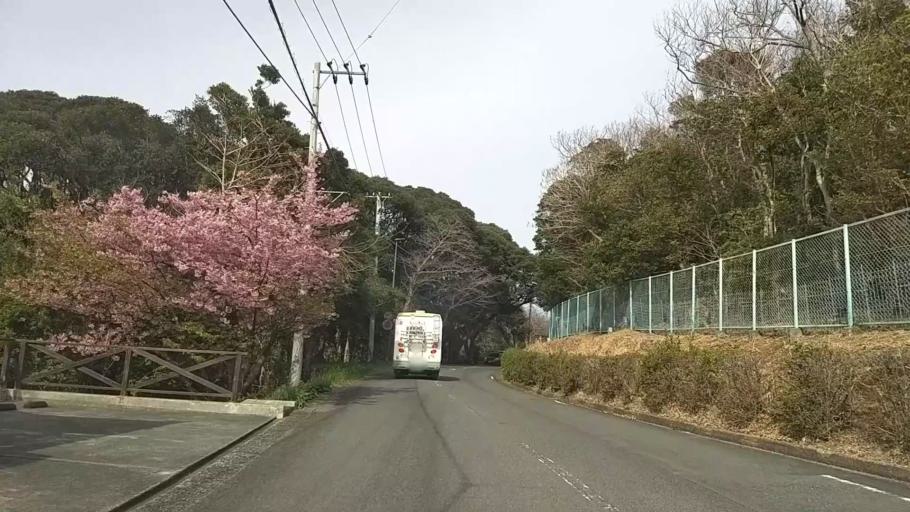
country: JP
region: Shizuoka
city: Shimoda
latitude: 34.6653
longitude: 138.9789
